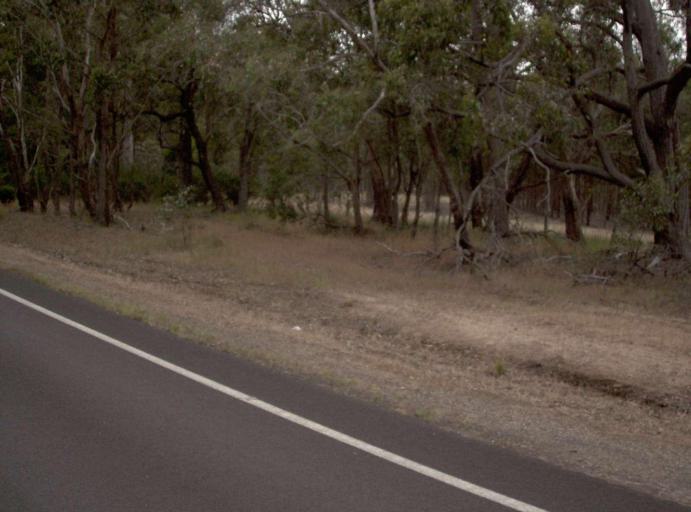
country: AU
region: Victoria
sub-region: Wellington
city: Sale
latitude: -38.4294
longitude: 146.9529
